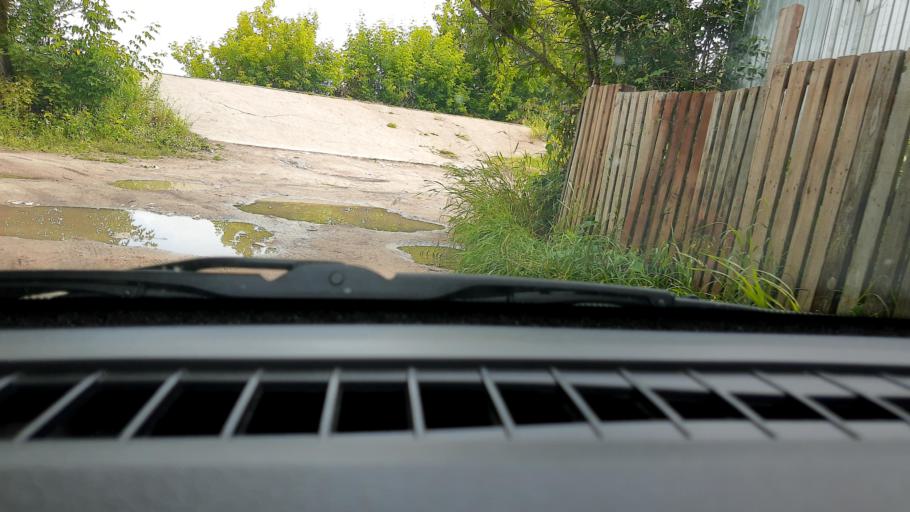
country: RU
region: Nizjnij Novgorod
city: Neklyudovo
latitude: 56.3990
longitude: 43.8492
